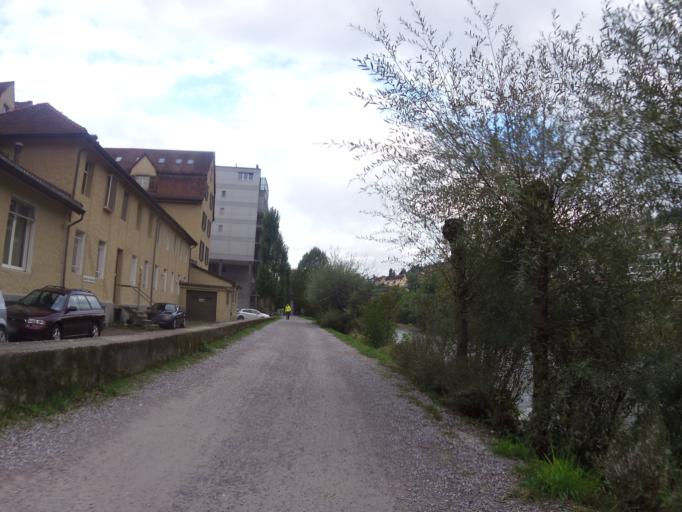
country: CH
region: Zurich
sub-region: Bezirk Zuerich
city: Zuerich (Kreis 5) / Escher-Wyss
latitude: 47.3929
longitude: 8.5168
